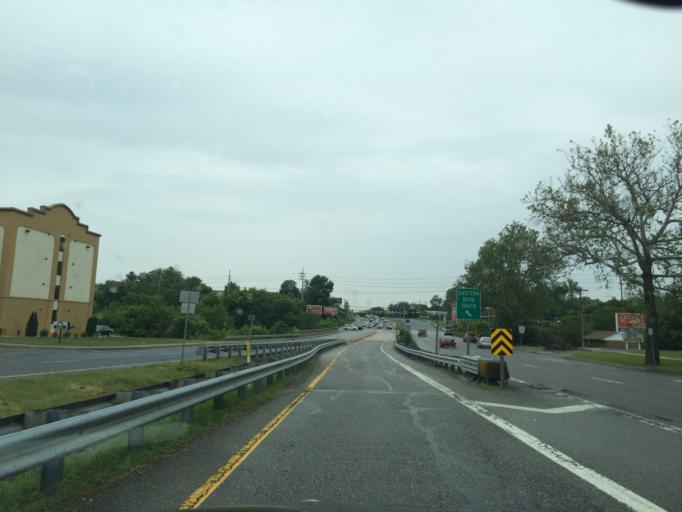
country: US
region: Maryland
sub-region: Washington County
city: Hagerstown
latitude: 39.6300
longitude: -77.7006
